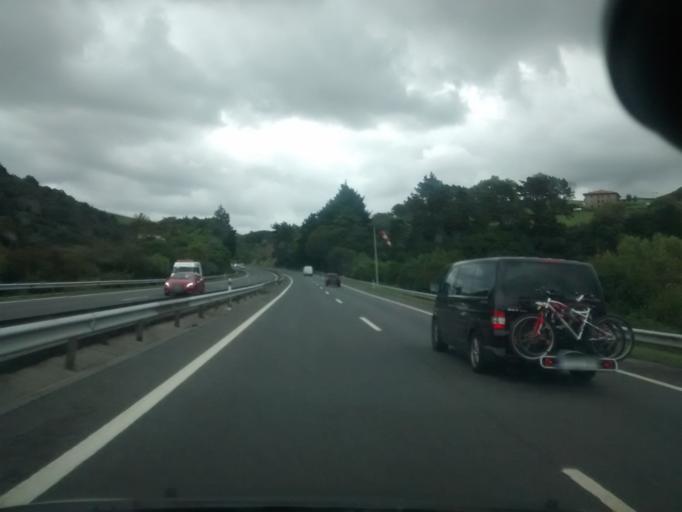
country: ES
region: Basque Country
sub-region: Provincia de Guipuzcoa
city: Orio
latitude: 43.2823
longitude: -2.1262
